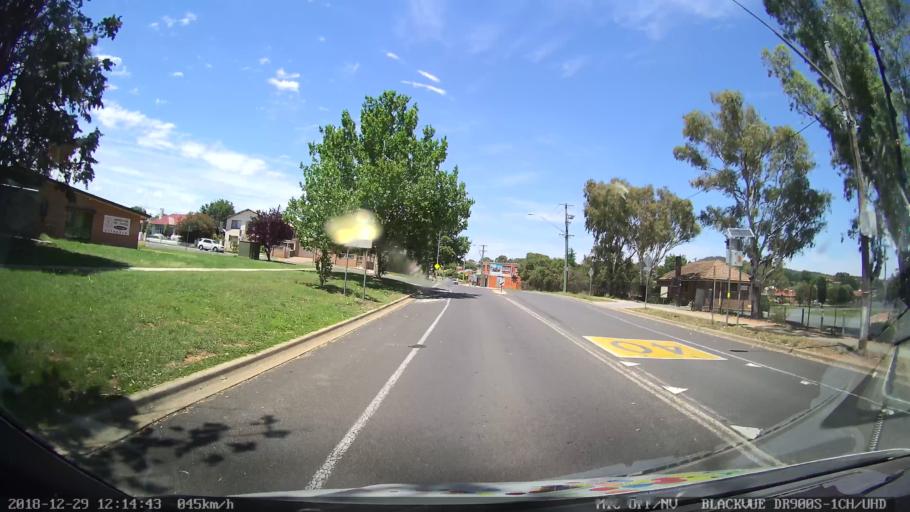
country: AU
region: New South Wales
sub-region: Queanbeyan
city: Queanbeyan
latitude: -35.3571
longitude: 149.2331
